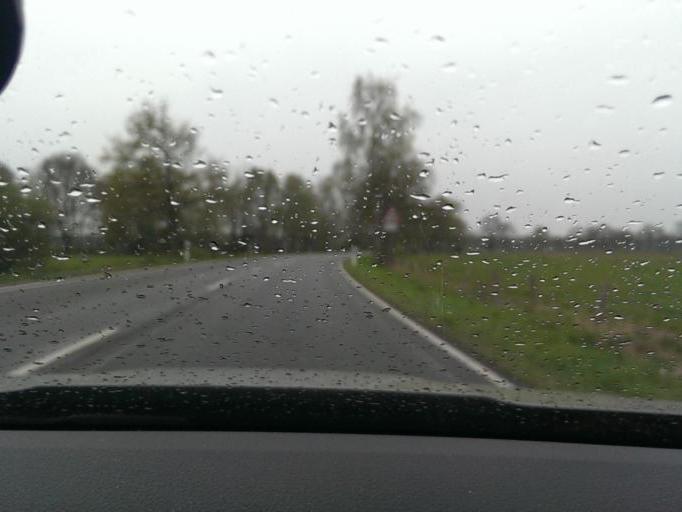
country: DE
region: Lower Saxony
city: Gilten
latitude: 52.6720
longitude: 9.5175
